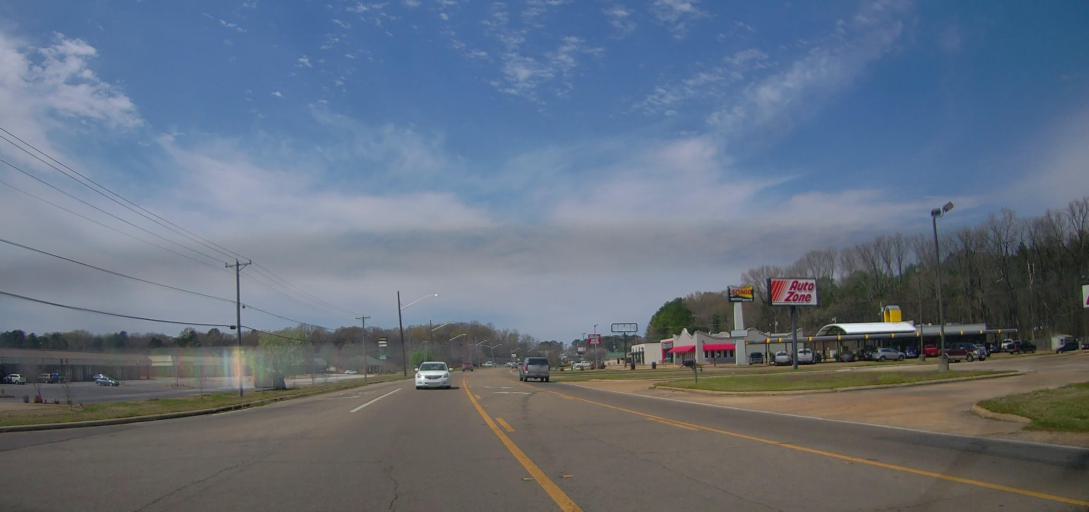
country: US
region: Mississippi
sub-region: Union County
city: New Albany
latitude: 34.4959
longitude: -89.0182
